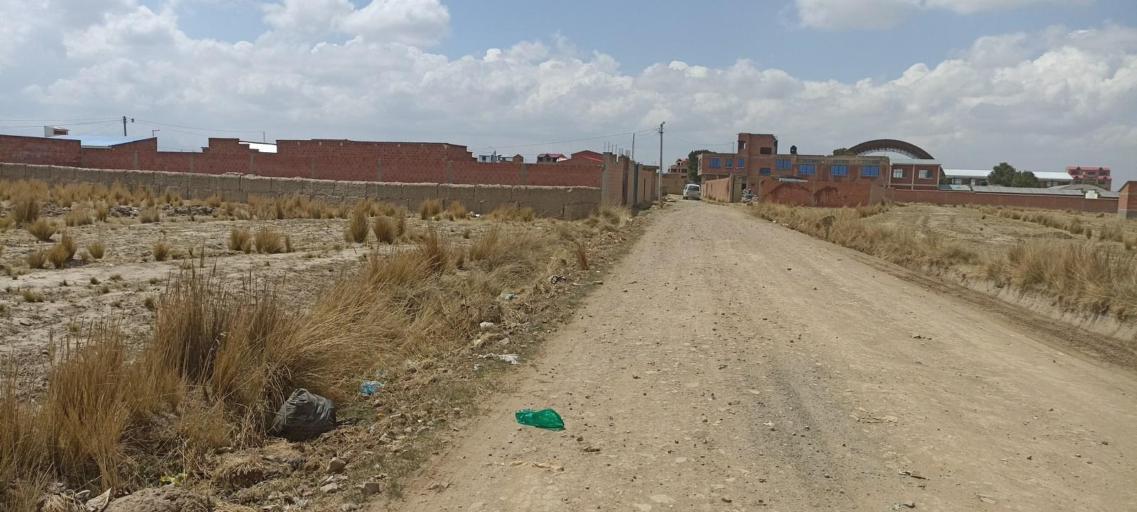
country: BO
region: La Paz
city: Batallas
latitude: -16.4089
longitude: -68.5440
